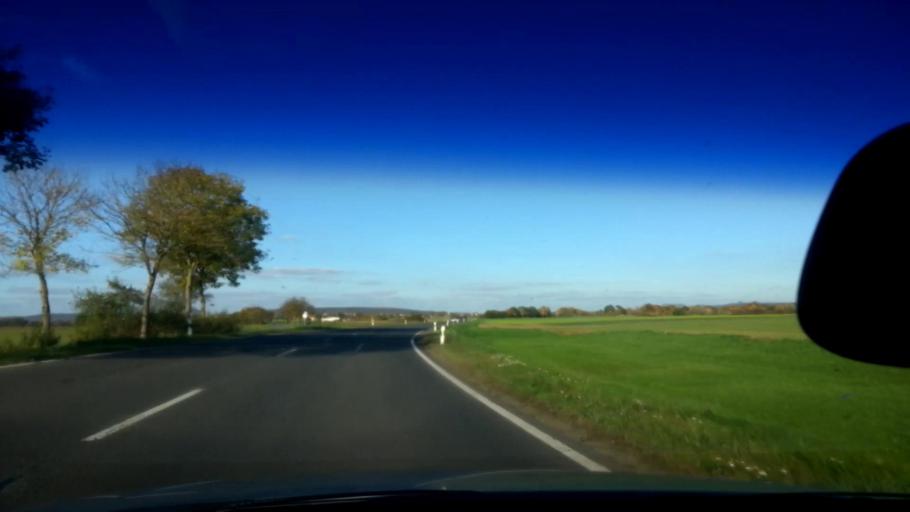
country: DE
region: Bavaria
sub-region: Upper Franconia
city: Rattelsdorf
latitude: 49.9960
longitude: 10.8830
